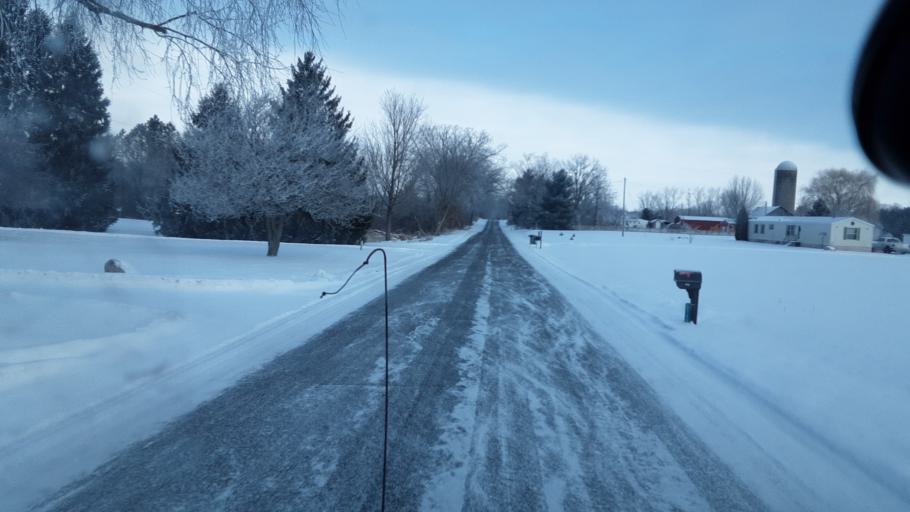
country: US
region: Michigan
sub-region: Ingham County
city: Leslie
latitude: 42.4437
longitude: -84.4970
